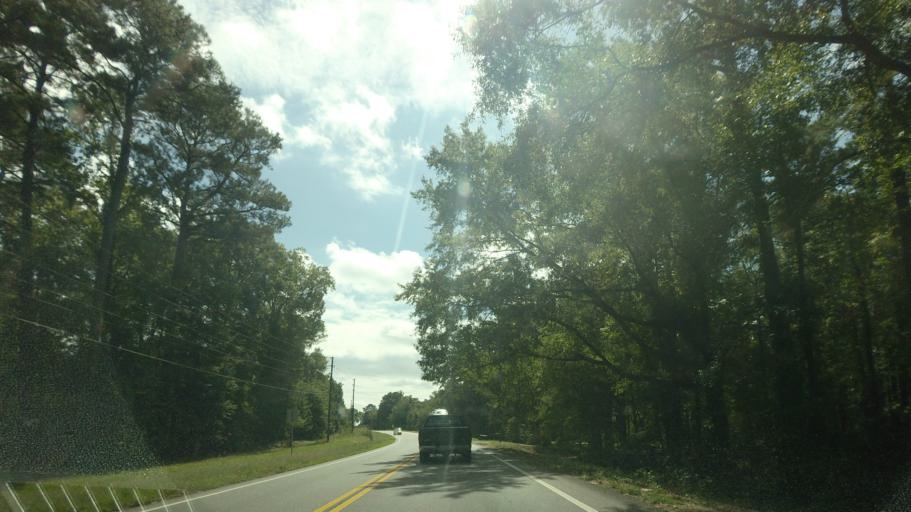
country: US
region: Georgia
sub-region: Houston County
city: Robins Air Force Base
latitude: 32.5455
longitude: -83.5931
